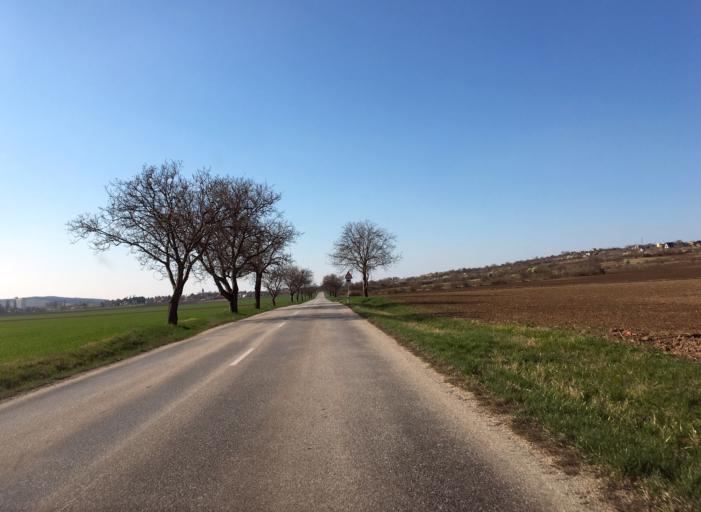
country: HU
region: Komarom-Esztergom
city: Nyergesujfalu
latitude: 47.8381
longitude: 18.5392
